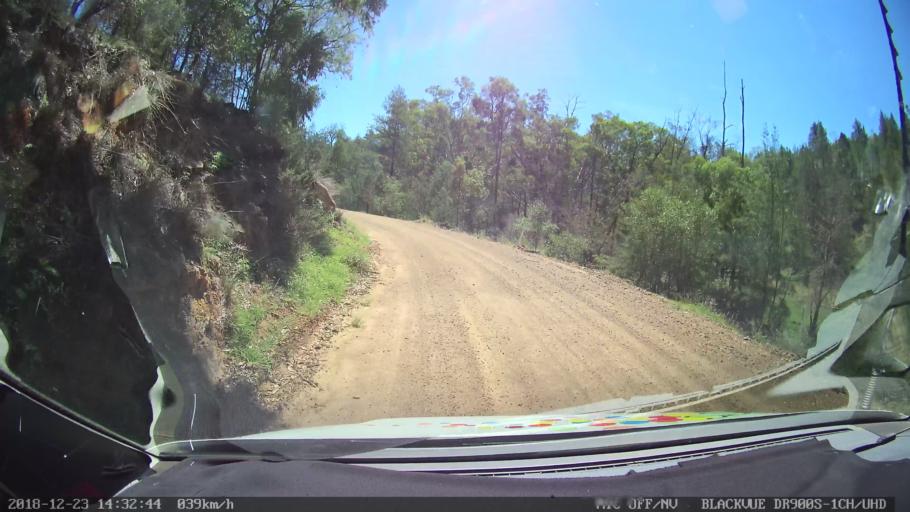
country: AU
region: New South Wales
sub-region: Tamworth Municipality
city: Manilla
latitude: -30.6043
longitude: 150.9163
